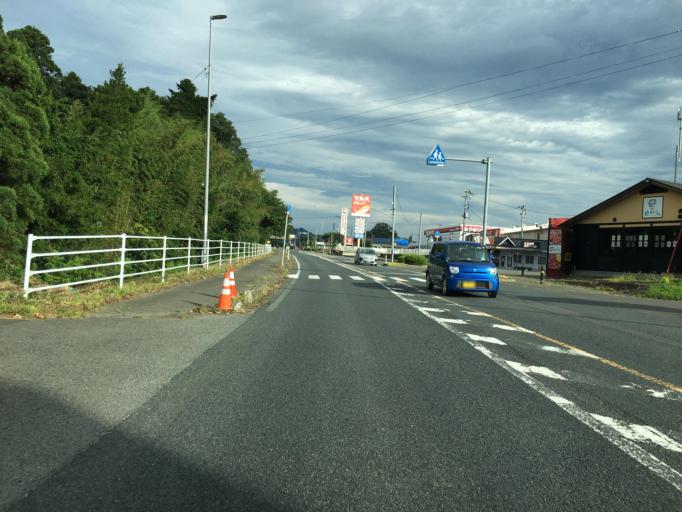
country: JP
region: Miyagi
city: Marumori
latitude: 37.8091
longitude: 140.9261
